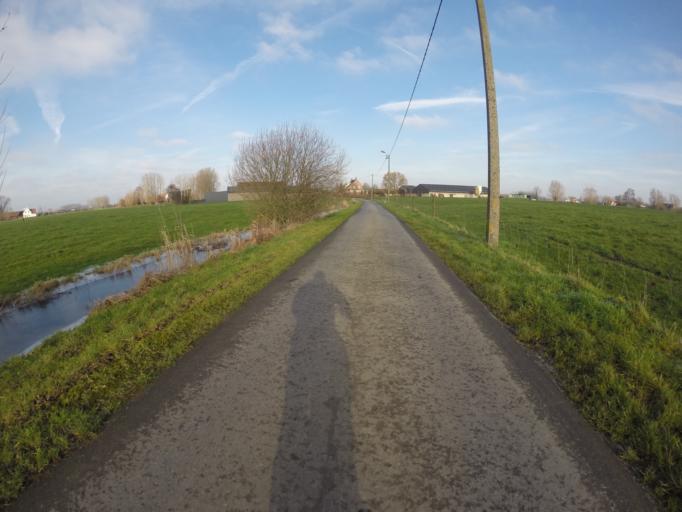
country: BE
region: Flanders
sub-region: Provincie Oost-Vlaanderen
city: Nevele
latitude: 51.0487
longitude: 3.5145
